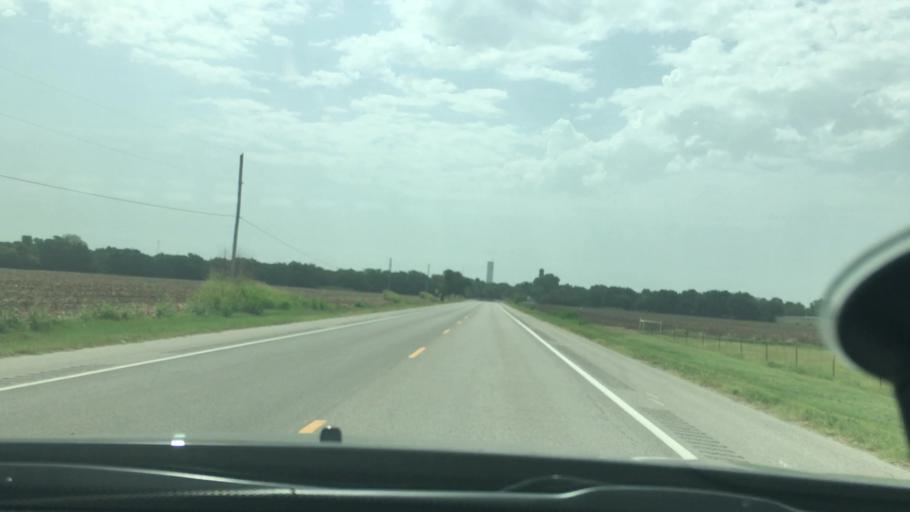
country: US
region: Oklahoma
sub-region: Garvin County
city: Pauls Valley
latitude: 34.8342
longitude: -97.2645
